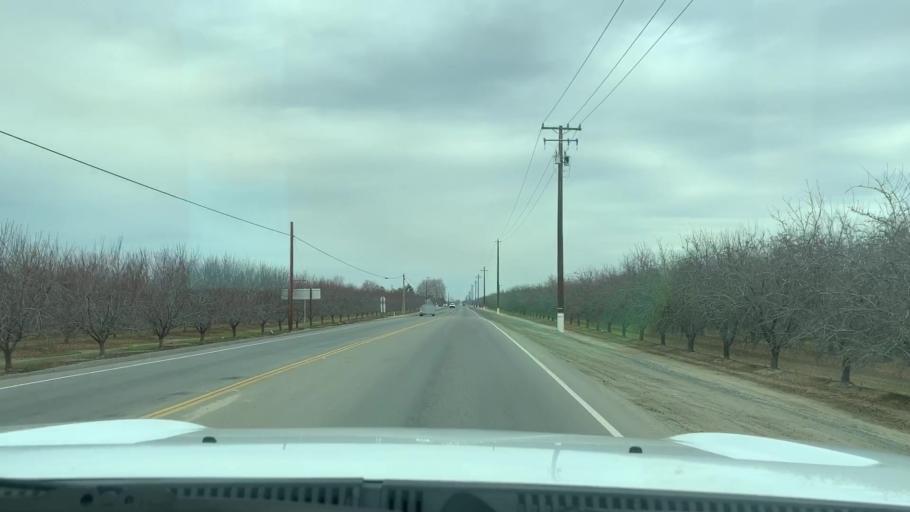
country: US
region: California
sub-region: Kern County
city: Shafter
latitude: 35.3985
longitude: -119.2520
